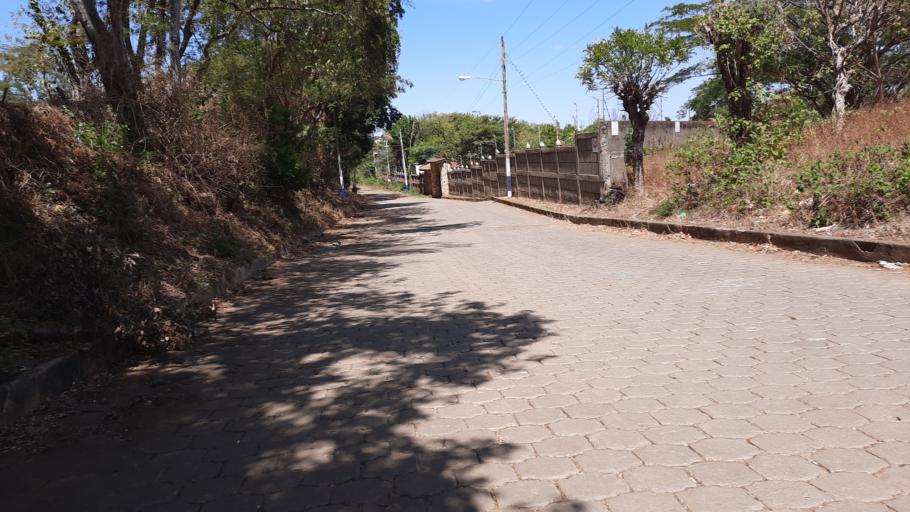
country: NI
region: Masaya
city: Ticuantepe
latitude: 12.0259
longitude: -86.1677
